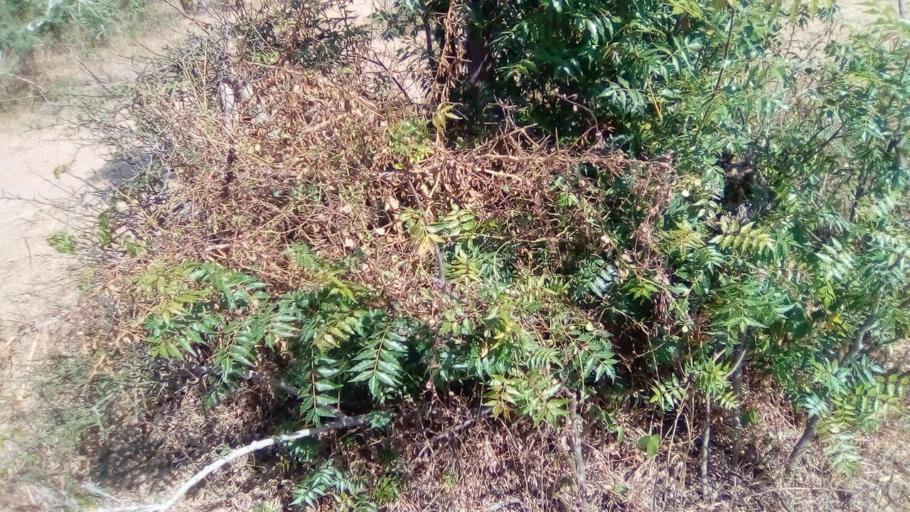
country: GH
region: Upper East
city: Bawku
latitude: 11.1102
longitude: -0.1404
